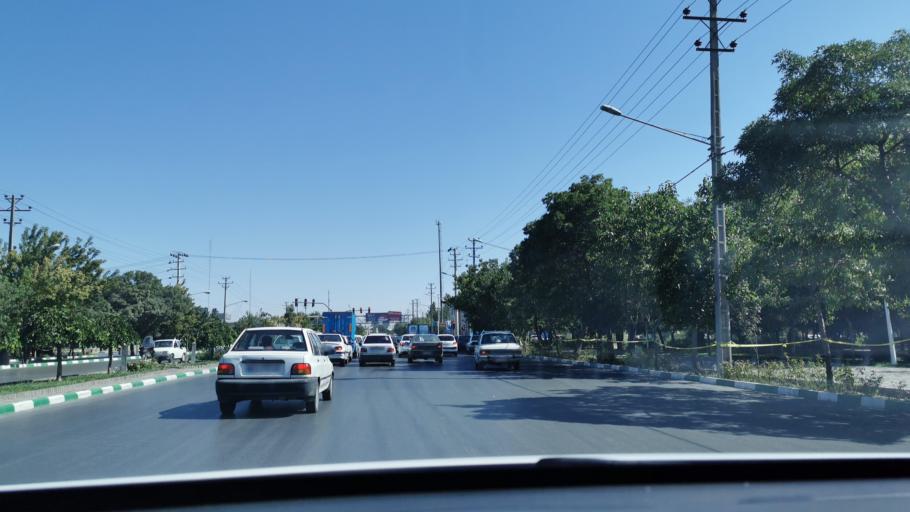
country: IR
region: Razavi Khorasan
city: Mashhad
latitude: 36.3352
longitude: 59.6258
